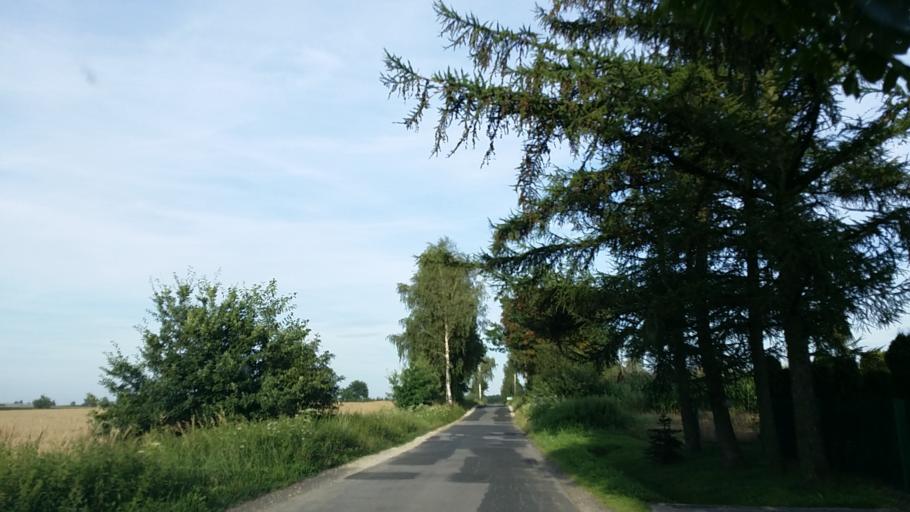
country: PL
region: Lesser Poland Voivodeship
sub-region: Powiat oswiecimski
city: Przeciszow
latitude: 49.9917
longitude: 19.3972
